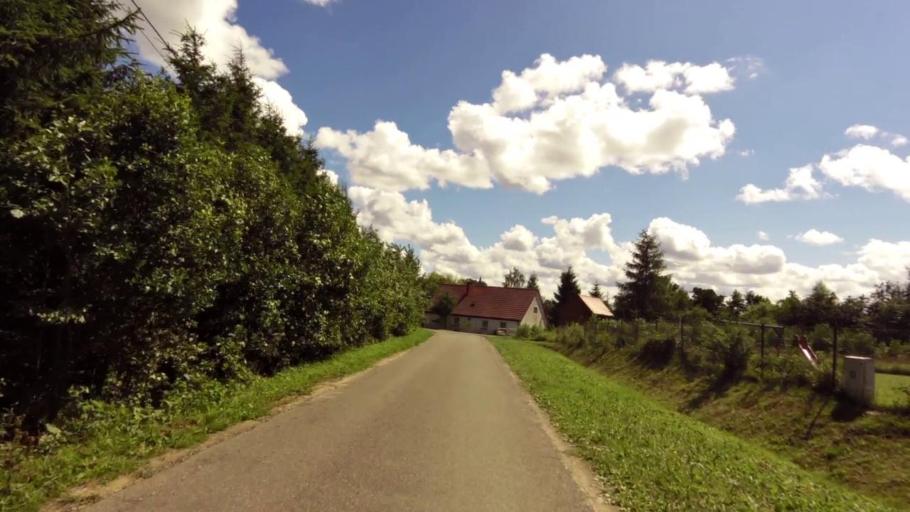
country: PL
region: West Pomeranian Voivodeship
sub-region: Powiat slawienski
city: Slawno
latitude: 54.5244
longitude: 16.6079
